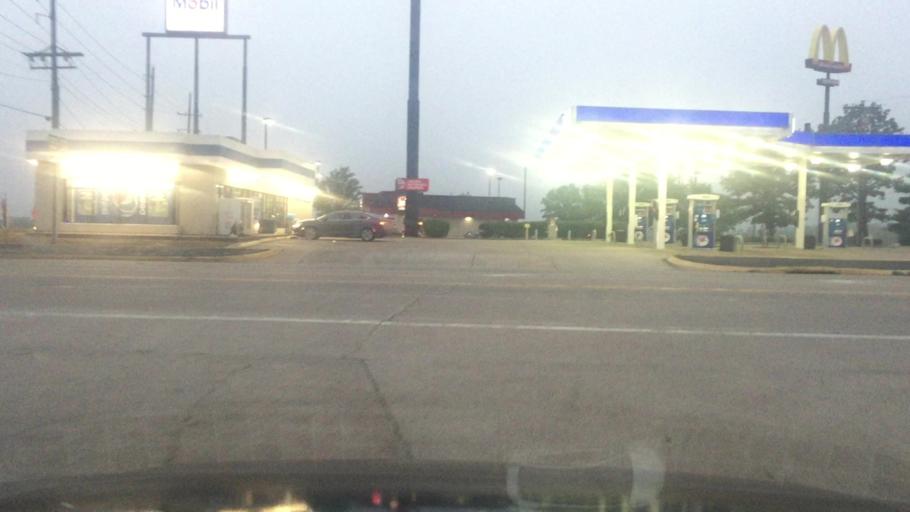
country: US
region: Missouri
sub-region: Warren County
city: Warrenton
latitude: 38.8225
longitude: -91.1383
